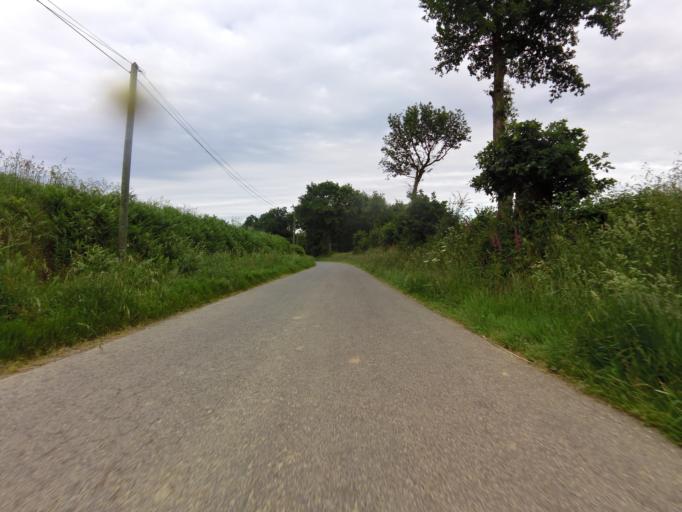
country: FR
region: Brittany
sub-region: Departement du Morbihan
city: Pluherlin
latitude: 47.7143
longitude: -2.3834
